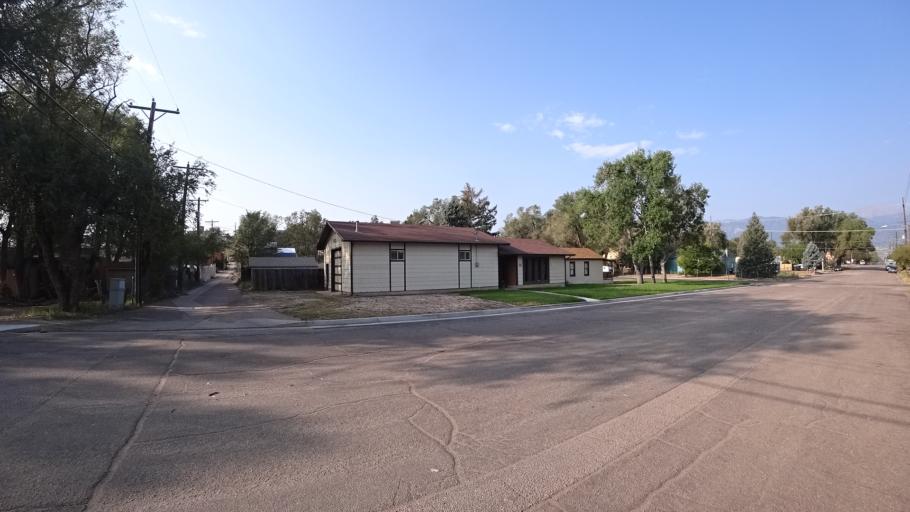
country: US
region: Colorado
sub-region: El Paso County
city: Colorado Springs
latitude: 38.8343
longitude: -104.7911
